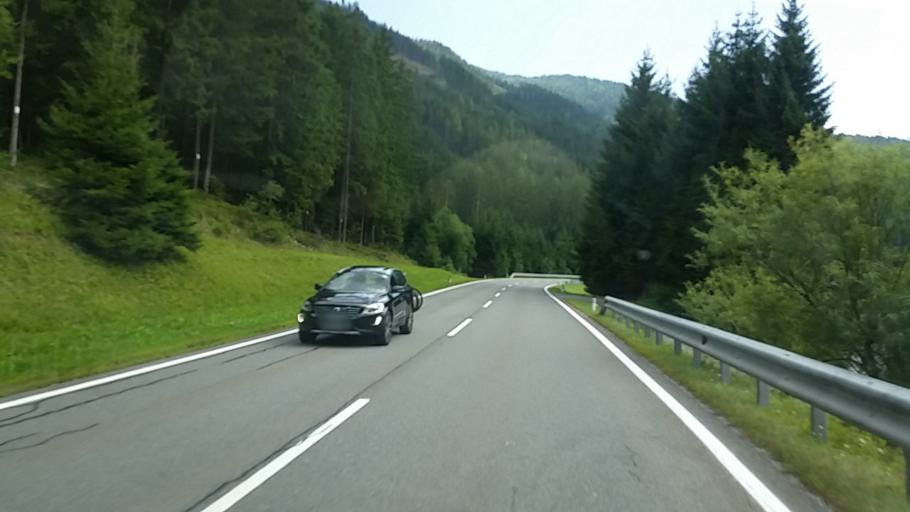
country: AT
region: Salzburg
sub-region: Politischer Bezirk Sankt Johann im Pongau
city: Untertauern
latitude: 47.3178
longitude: 13.5093
